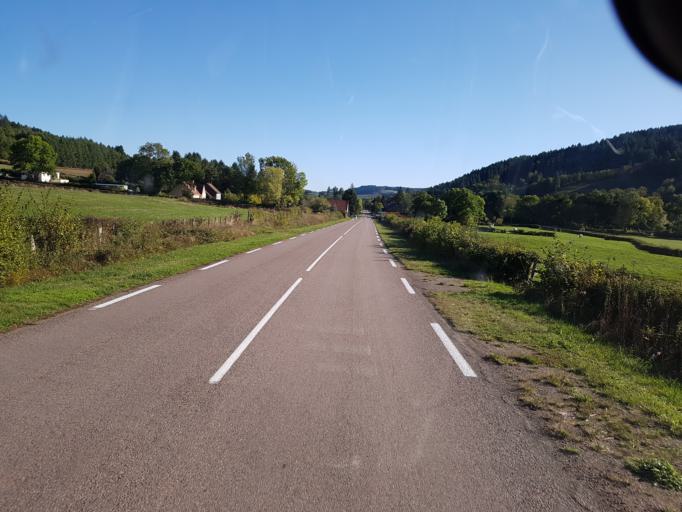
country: FR
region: Bourgogne
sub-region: Departement de Saone-et-Loire
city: Autun
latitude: 47.0908
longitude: 4.2390
